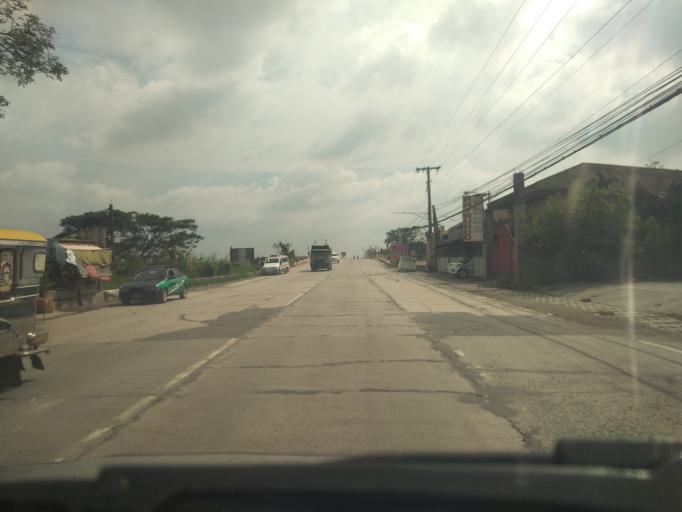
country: PH
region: Central Luzon
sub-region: Province of Pampanga
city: Santo Domingo
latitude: 15.0002
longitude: 120.7286
